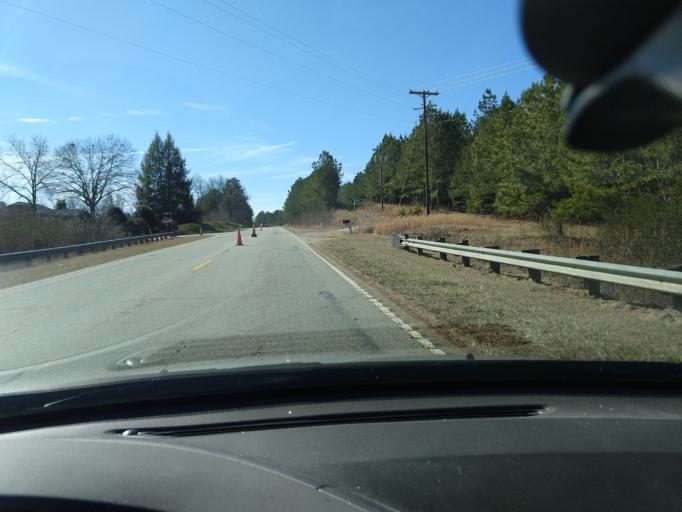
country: US
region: South Carolina
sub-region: Oconee County
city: Westminster
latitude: 34.6643
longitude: -83.1240
